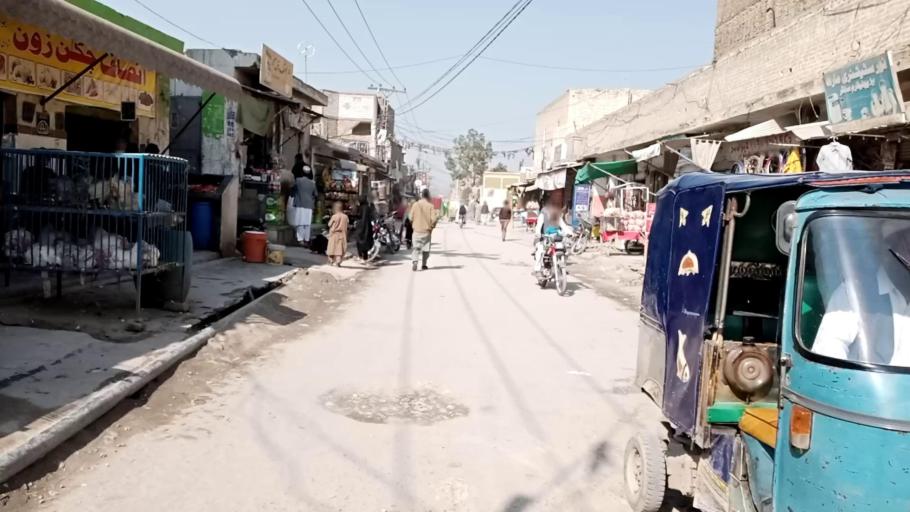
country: PK
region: Khyber Pakhtunkhwa
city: Peshawar
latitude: 34.0097
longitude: 71.5181
